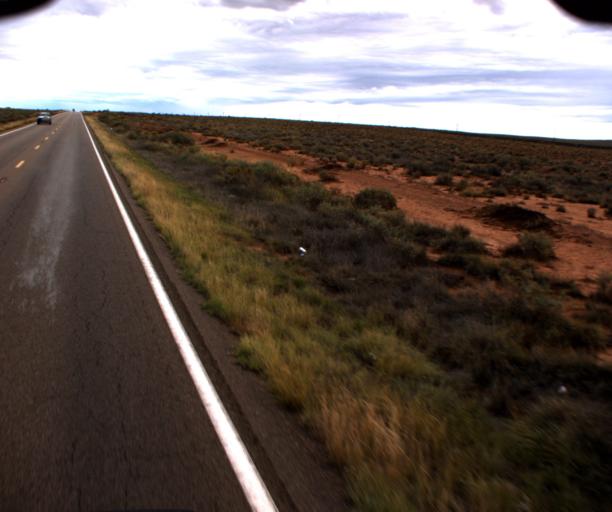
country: US
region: Arizona
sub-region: Navajo County
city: Holbrook
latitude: 34.8186
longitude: -110.1402
